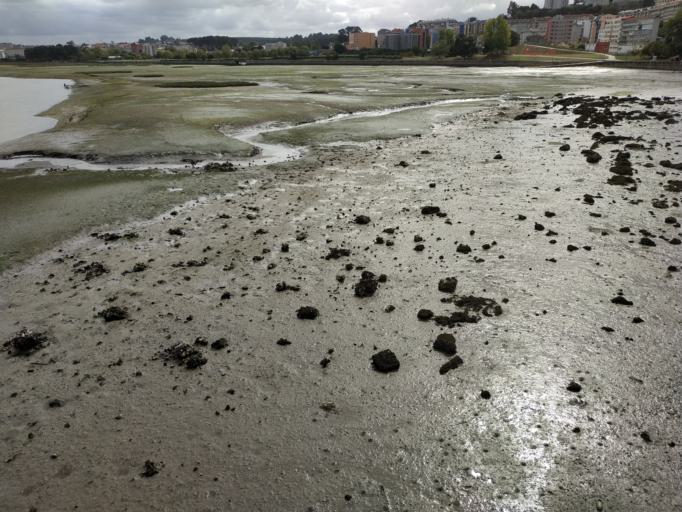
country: ES
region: Galicia
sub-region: Provincia da Coruna
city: Culleredo
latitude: 43.3279
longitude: -8.3789
